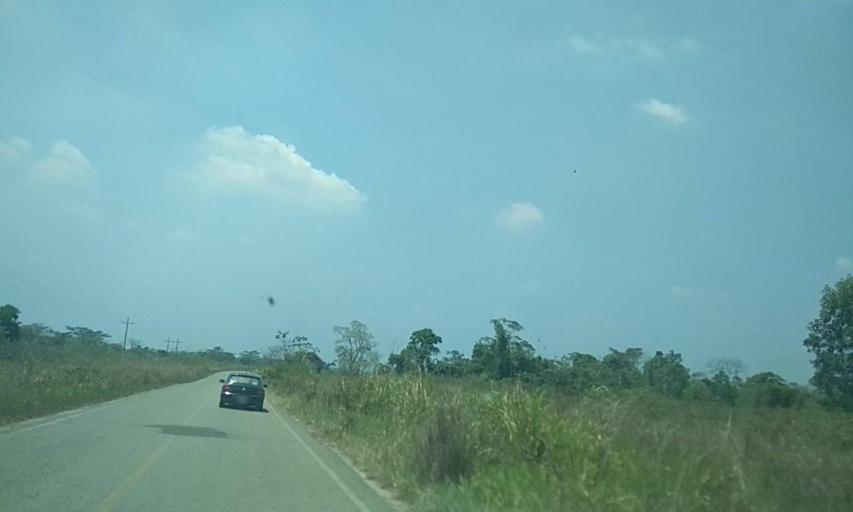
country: MX
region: Tabasco
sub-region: Huimanguillo
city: Paso de la Mina 3ra. Seccion
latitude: 17.8240
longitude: -93.6170
